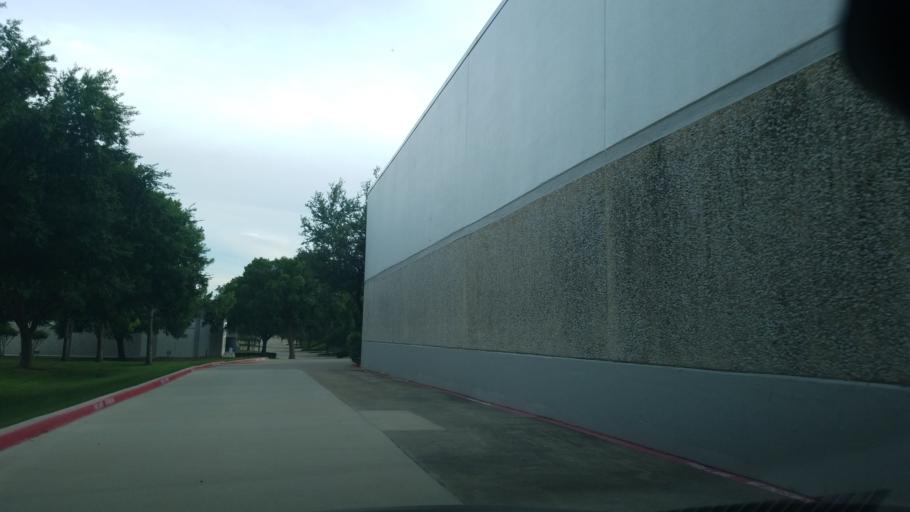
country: US
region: Texas
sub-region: Dallas County
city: Irving
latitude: 32.8722
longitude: -96.9877
